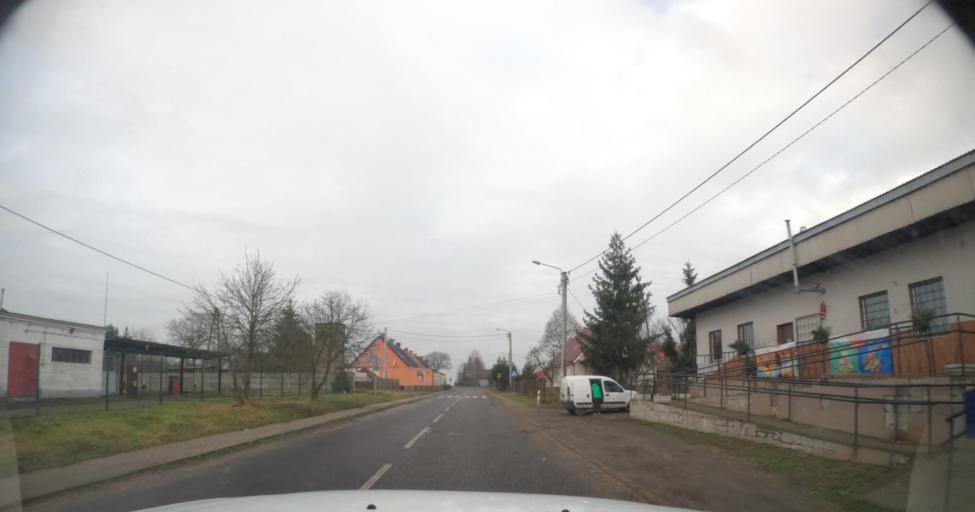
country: PL
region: West Pomeranian Voivodeship
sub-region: Powiat mysliborski
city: Boleszkowice
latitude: 52.7419
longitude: 14.6092
